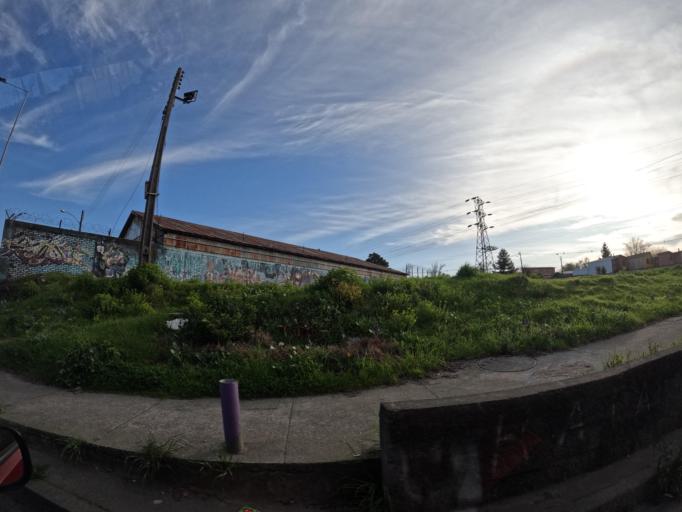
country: CL
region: Biobio
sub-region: Provincia de Concepcion
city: Concepcion
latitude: -36.8012
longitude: -73.0307
